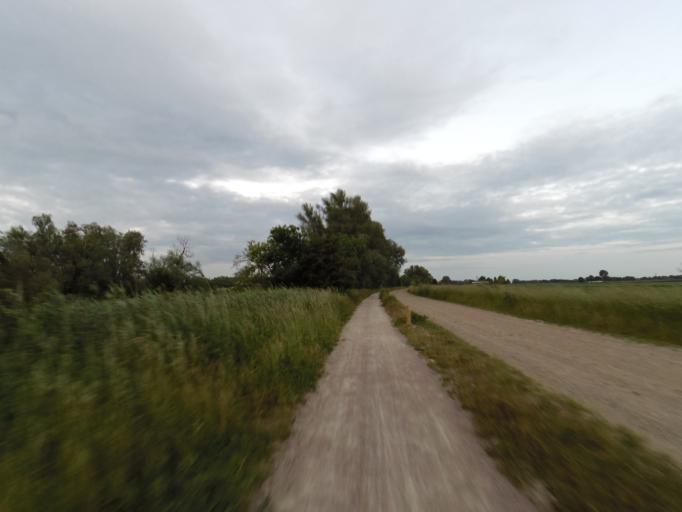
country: NL
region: Gelderland
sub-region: Gemeente Zevenaar
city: Zevenaar
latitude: 51.8833
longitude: 6.1298
